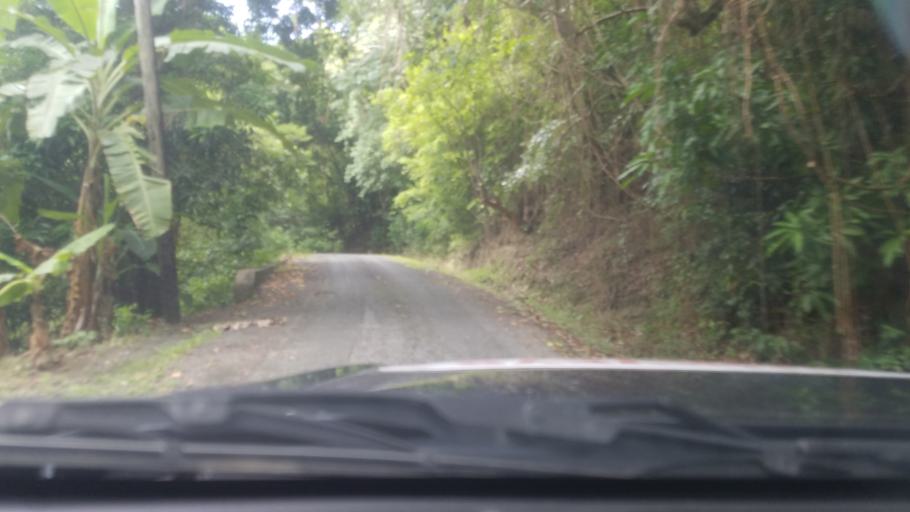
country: LC
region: Praslin
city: Praslin
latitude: 13.8620
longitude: -60.9054
